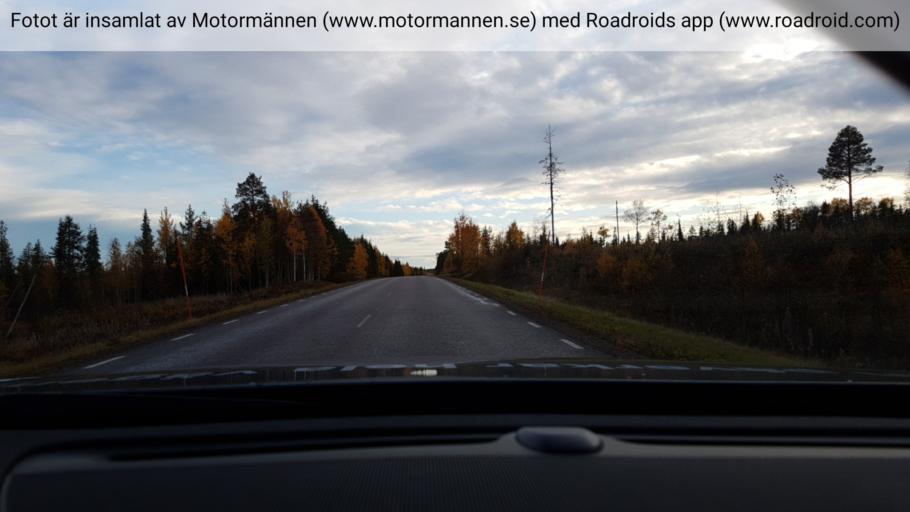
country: SE
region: Norrbotten
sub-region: Overkalix Kommun
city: OEverkalix
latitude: 66.8913
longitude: 22.7700
